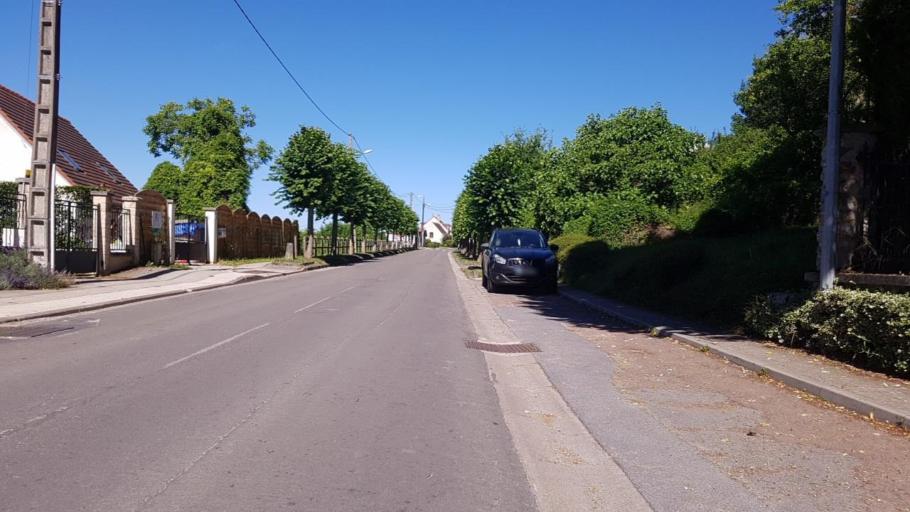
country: FR
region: Picardie
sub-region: Departement de l'Aisne
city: Charly-sur-Marne
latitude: 48.9722
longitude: 3.3158
